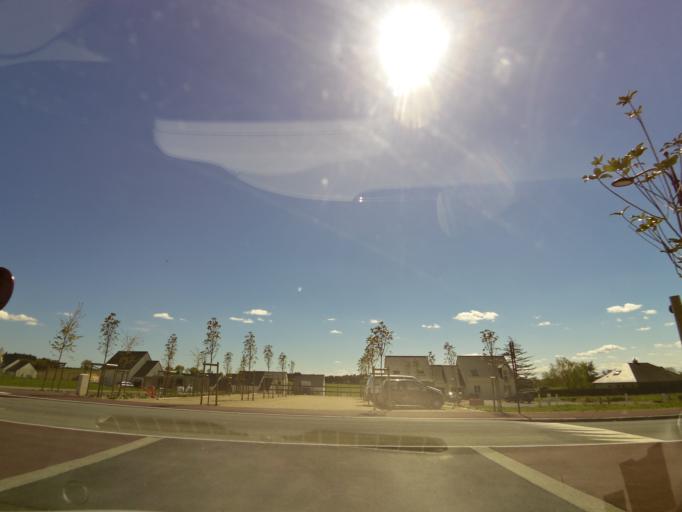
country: FR
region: Brittany
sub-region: Departement d'Ille-et-Vilaine
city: Tresboeuf
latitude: 47.9150
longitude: -1.5864
